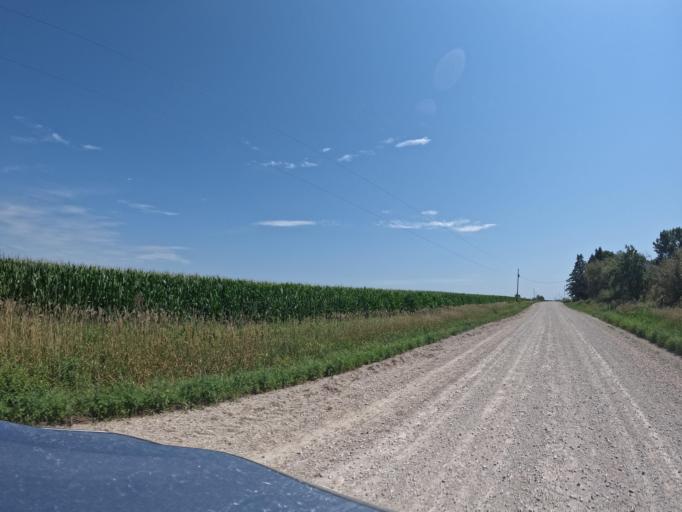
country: US
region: Iowa
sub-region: Henry County
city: Mount Pleasant
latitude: 40.8956
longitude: -91.6317
